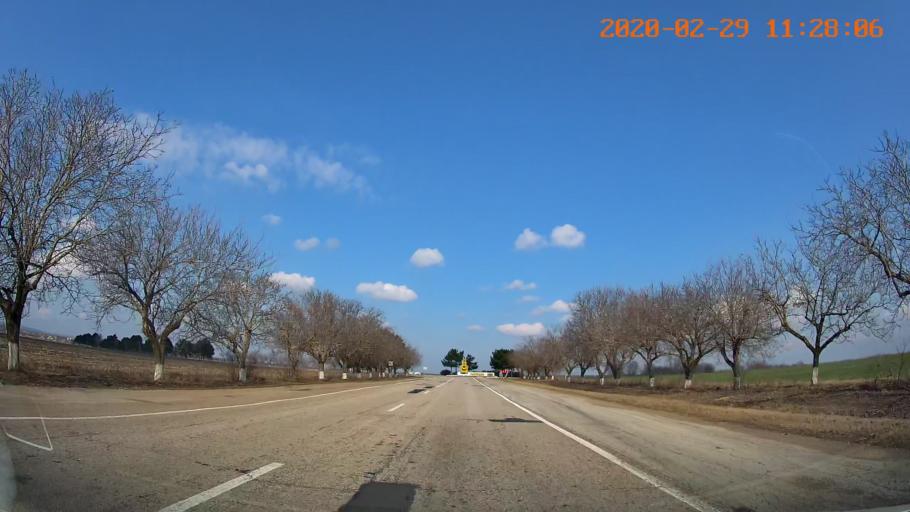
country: MD
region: Telenesti
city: Cocieri
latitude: 47.4784
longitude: 29.1397
